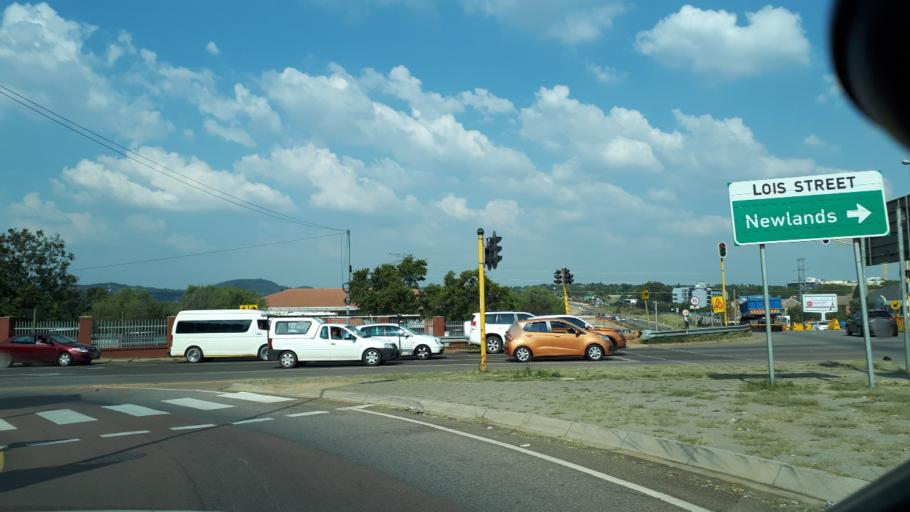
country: ZA
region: Gauteng
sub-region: City of Tshwane Metropolitan Municipality
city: Pretoria
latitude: -25.7813
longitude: 28.2776
